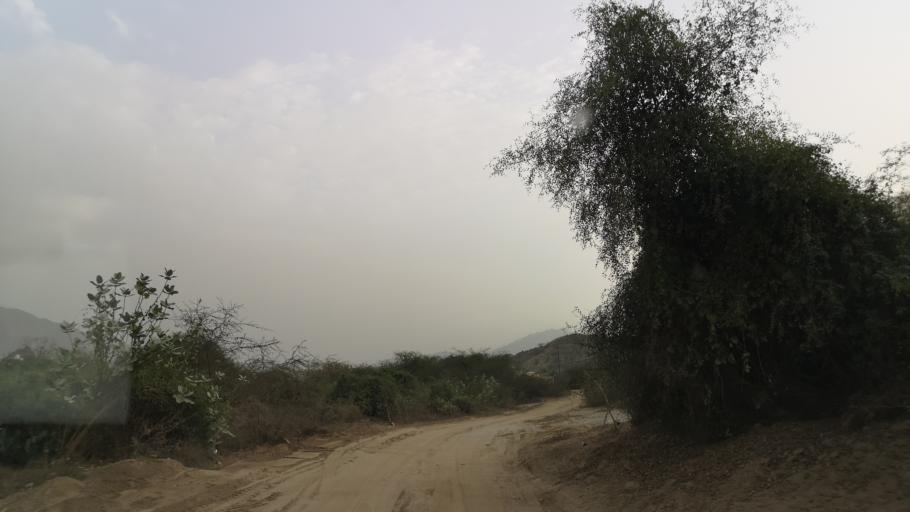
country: YE
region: Sa'dah
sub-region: Monabbih
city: Suq al Khamis
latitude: 17.3699
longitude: 43.1277
